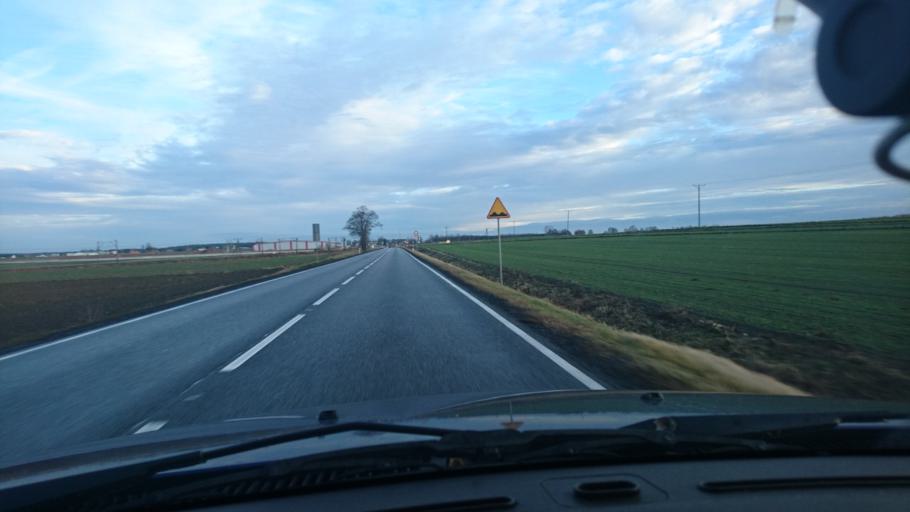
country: PL
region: Greater Poland Voivodeship
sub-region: Powiat kepinski
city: Slupia pod Kepnem
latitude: 51.2339
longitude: 18.0599
